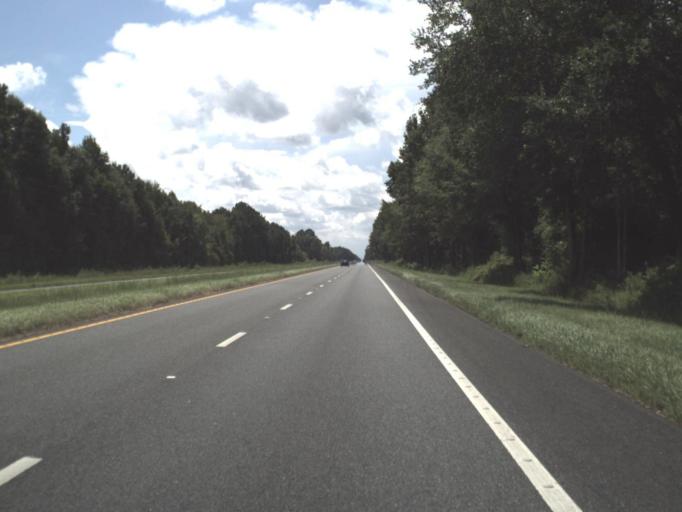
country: US
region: Florida
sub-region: Taylor County
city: Perry
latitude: 30.2724
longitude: -83.7202
